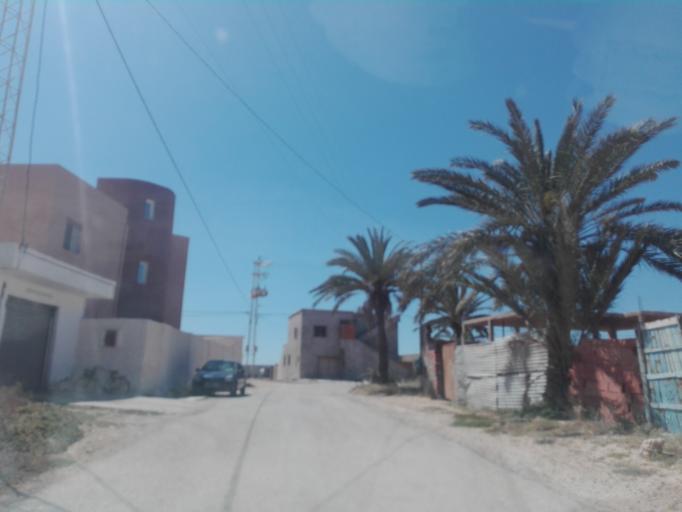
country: TN
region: Safaqis
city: Jabinyanah
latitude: 34.7402
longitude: 11.2989
